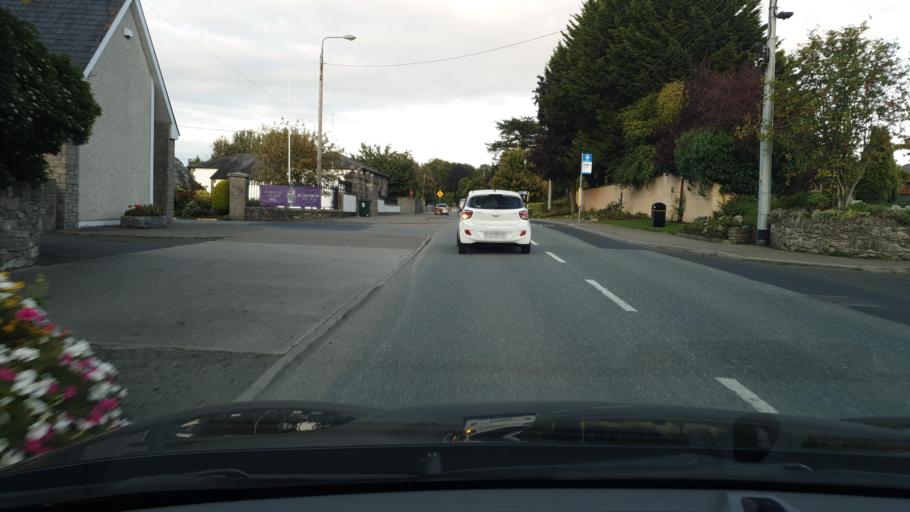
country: IE
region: Leinster
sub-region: Kildare
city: Kill
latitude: 53.2492
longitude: -6.5893
